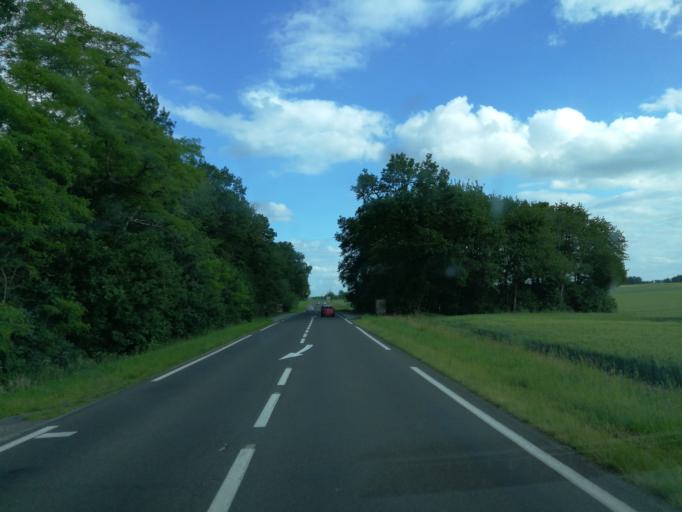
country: FR
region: Haute-Normandie
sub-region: Departement de l'Eure
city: Le Neubourg
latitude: 49.1135
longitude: 0.9129
